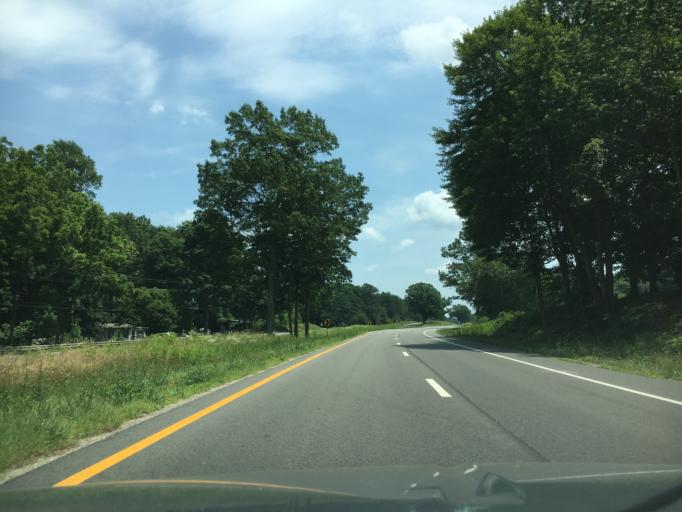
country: US
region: Virginia
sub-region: Buckingham County
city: Buckingham
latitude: 37.5460
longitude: -78.5204
